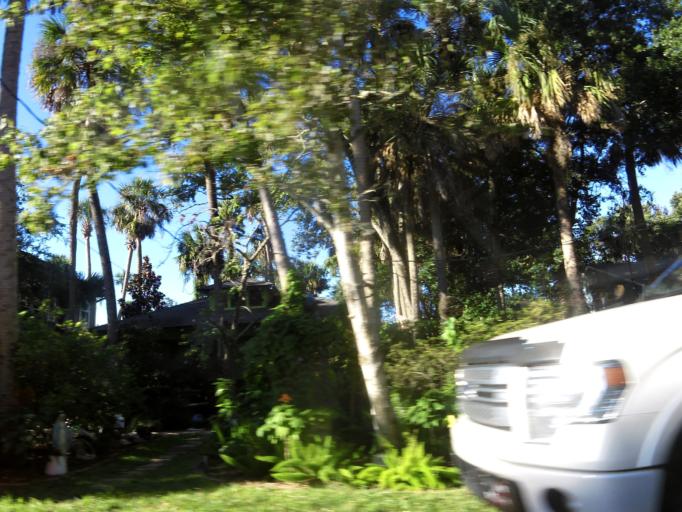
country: US
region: Florida
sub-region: Duval County
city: Atlantic Beach
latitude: 30.3289
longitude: -81.3991
